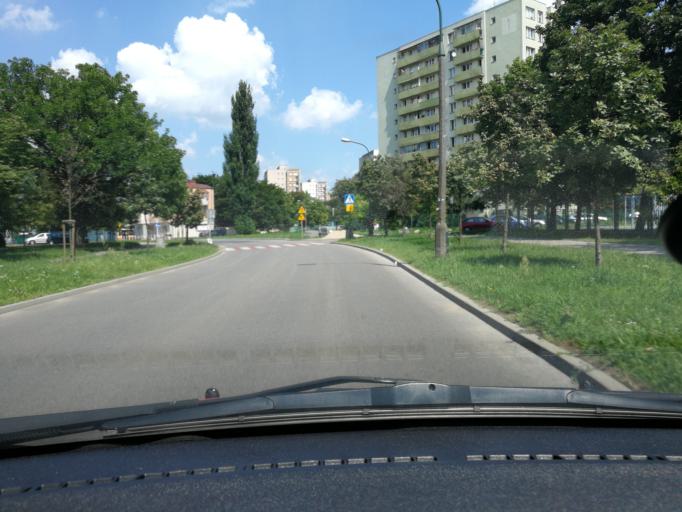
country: PL
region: Masovian Voivodeship
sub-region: Warszawa
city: Targowek
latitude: 52.2914
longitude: 21.0242
